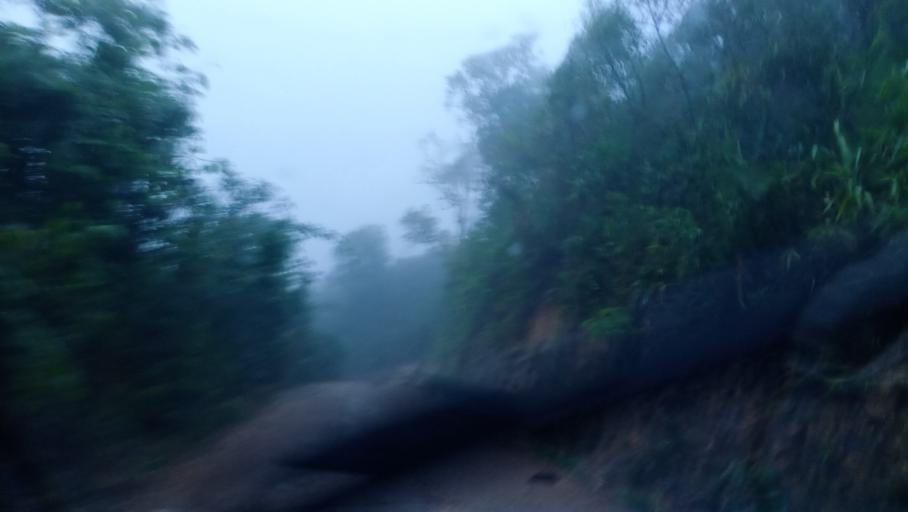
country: LA
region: Phongsali
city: Khoa
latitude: 21.2040
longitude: 102.2602
